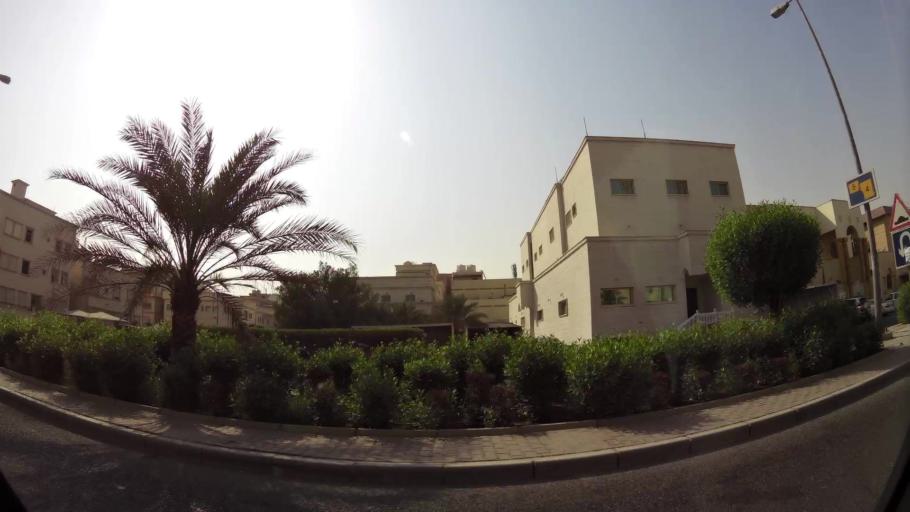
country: KW
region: Al Asimah
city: Ar Rabiyah
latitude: 29.2710
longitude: 47.8883
